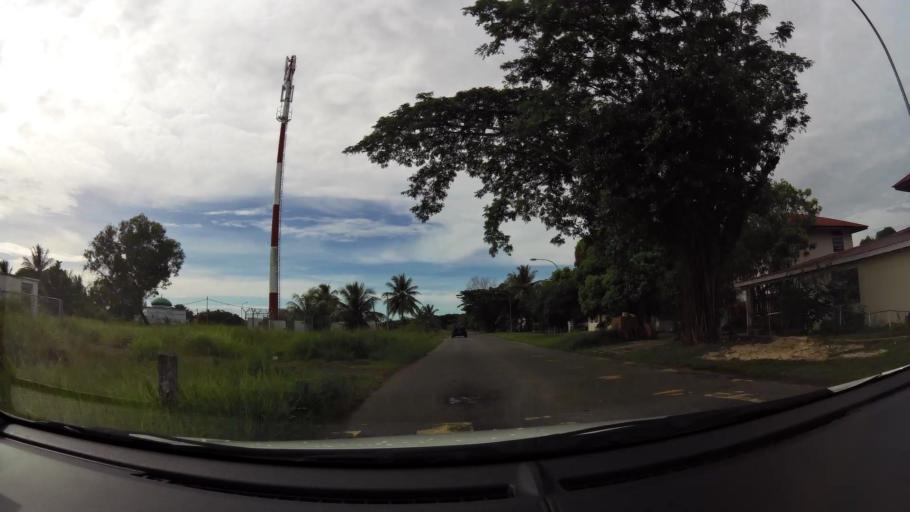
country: BN
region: Belait
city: Seria
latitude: 4.6013
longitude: 114.3264
